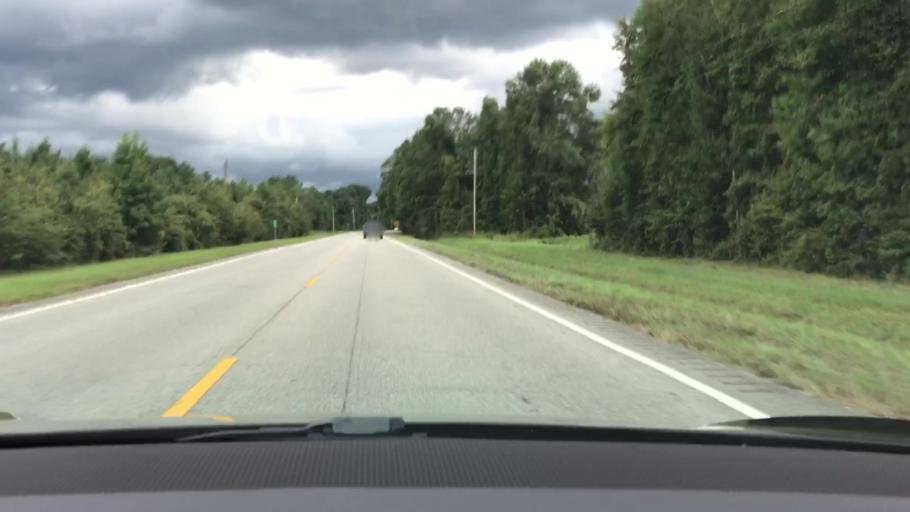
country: US
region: Alabama
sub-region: Coffee County
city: Elba
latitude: 31.4934
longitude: -86.0528
